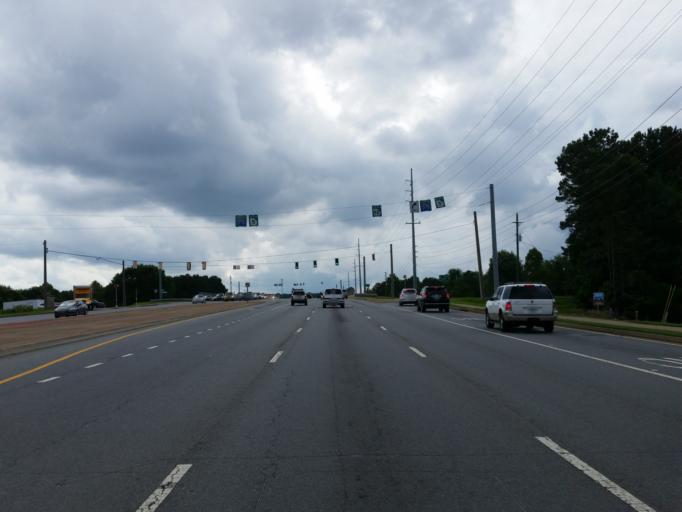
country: US
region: Georgia
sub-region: Cherokee County
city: Woodstock
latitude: 34.0859
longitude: -84.5330
